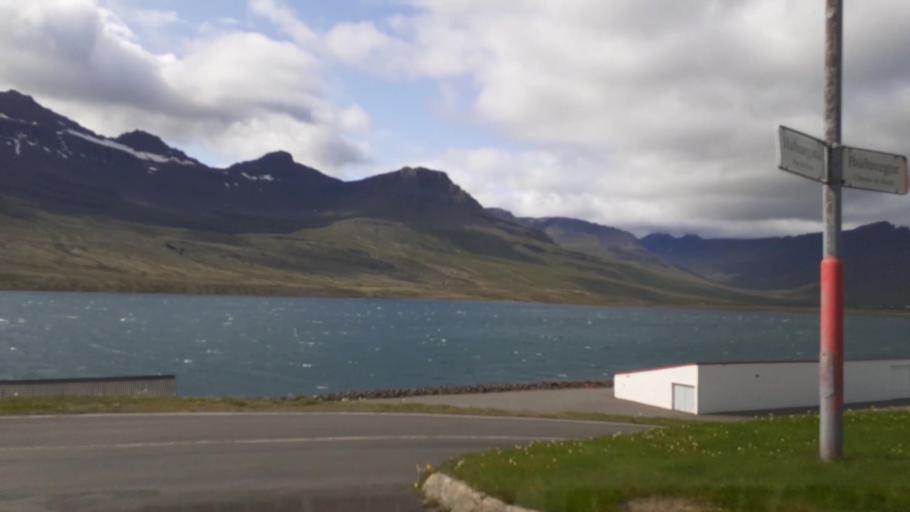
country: IS
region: East
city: Eskifjoerdur
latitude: 64.9276
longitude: -14.0042
